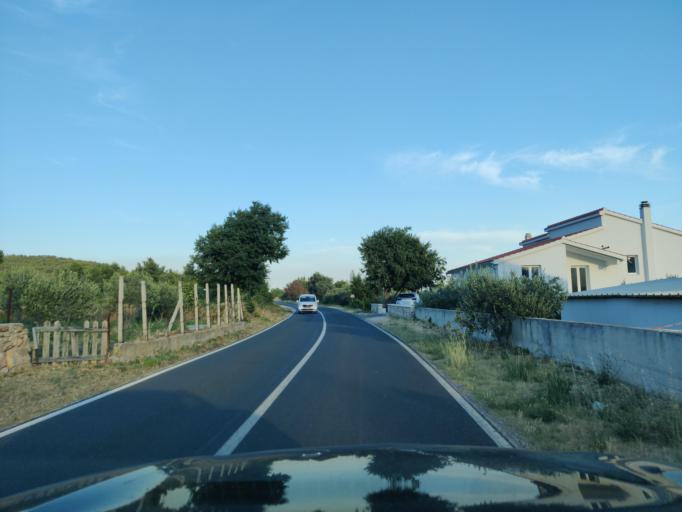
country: HR
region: Sibensko-Kniniska
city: Tribunj
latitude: 43.7668
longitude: 15.7333
